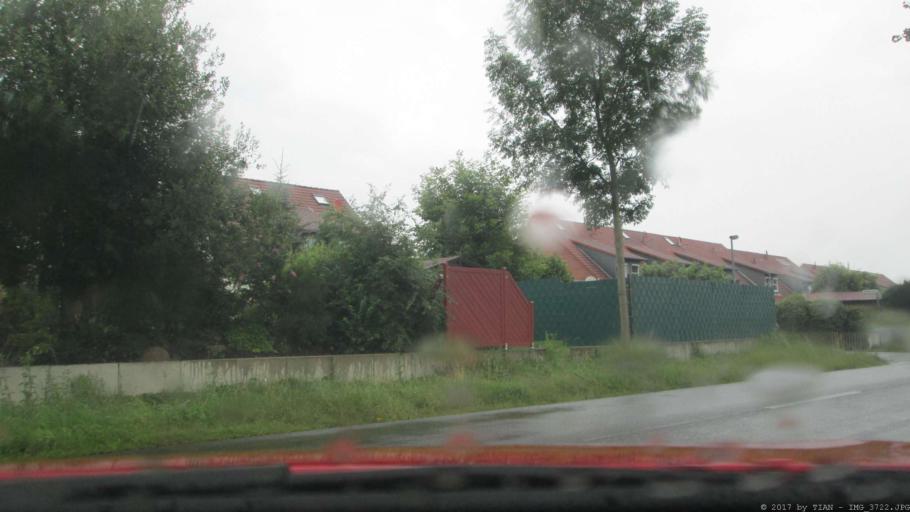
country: DE
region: Lower Saxony
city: Lehre
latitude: 52.3596
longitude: 10.7393
